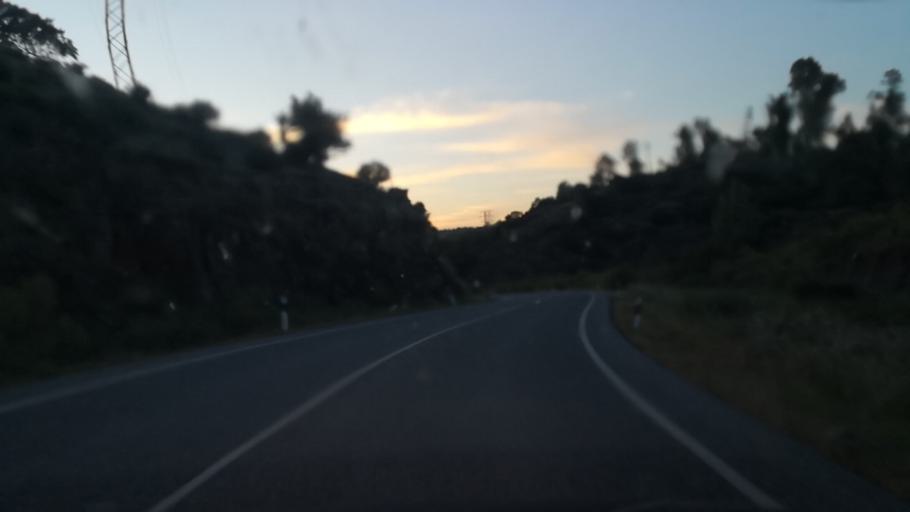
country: ES
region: Extremadura
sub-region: Provincia de Caceres
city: Alcantara
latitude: 39.7218
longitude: -6.8831
